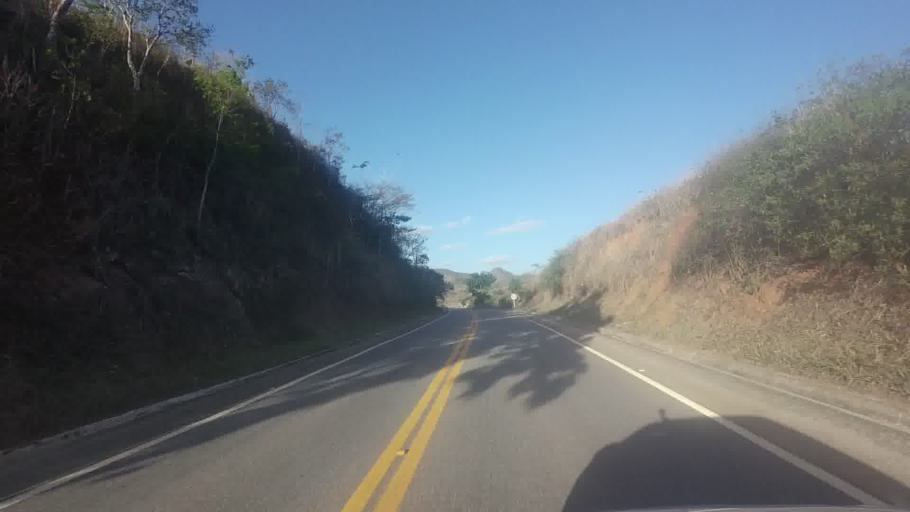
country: BR
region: Espirito Santo
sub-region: Jeronimo Monteiro
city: Jeronimo Monteiro
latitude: -20.8864
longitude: -41.2760
